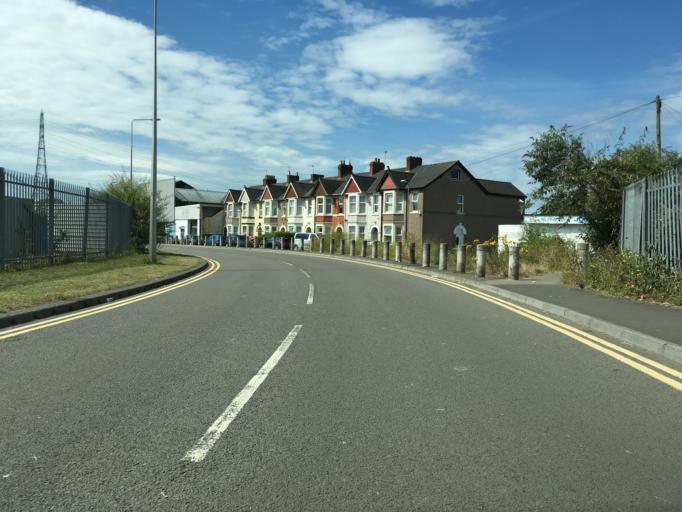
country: GB
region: Wales
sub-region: Newport
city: Newport
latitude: 51.5744
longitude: -2.9861
